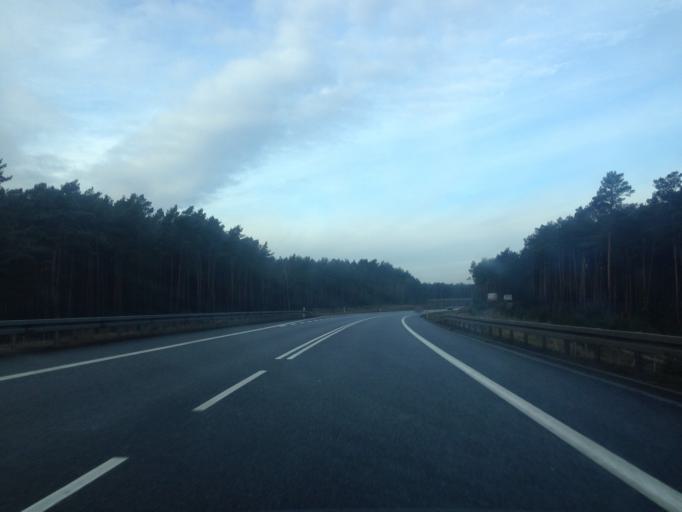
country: PL
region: Kujawsko-Pomorskie
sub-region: Powiat torunski
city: Wielka Nieszawka
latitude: 52.9676
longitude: 18.5472
